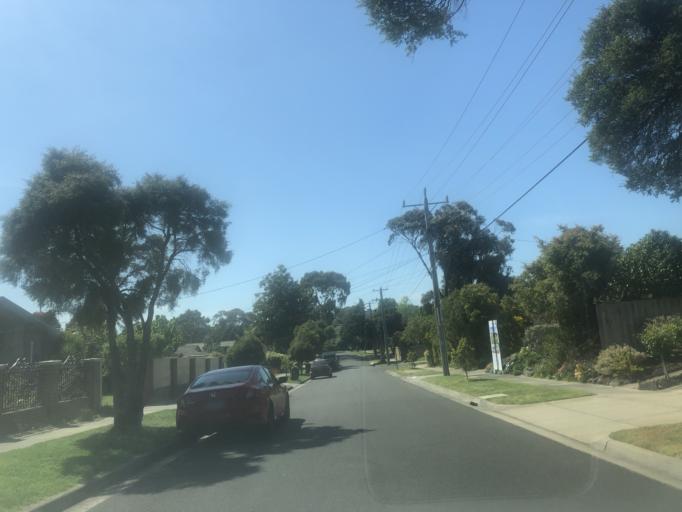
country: AU
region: Victoria
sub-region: Monash
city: Notting Hill
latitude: -37.9039
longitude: 145.1712
